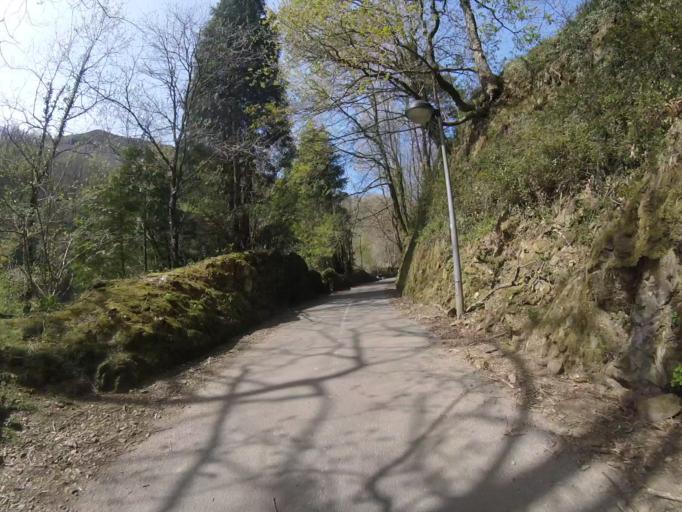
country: ES
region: Basque Country
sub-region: Provincia de Guipuzcoa
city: Irun
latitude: 43.2831
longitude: -1.8208
